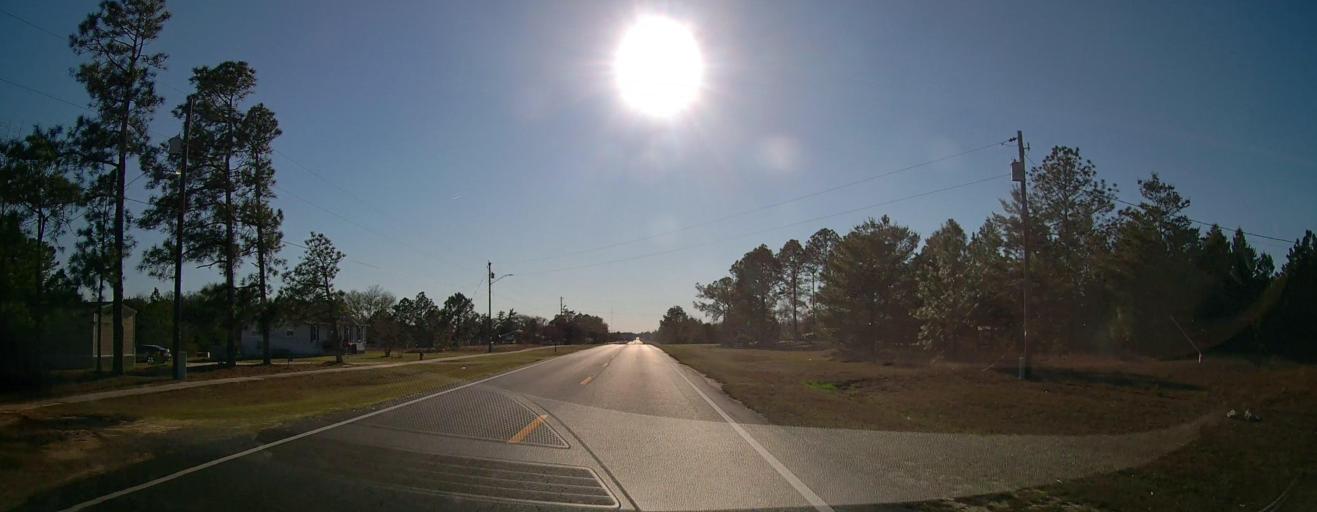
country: US
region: Georgia
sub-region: Taylor County
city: Butler
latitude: 32.5575
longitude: -84.2500
